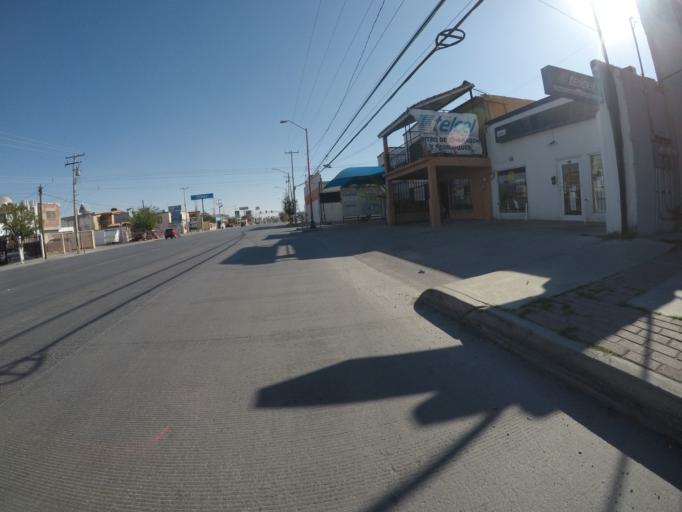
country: MX
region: Chihuahua
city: Ciudad Juarez
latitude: 31.7231
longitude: -106.4509
